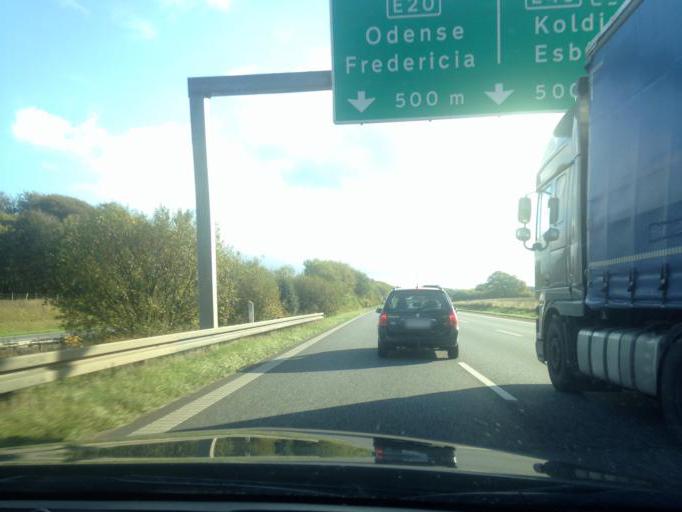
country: DK
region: South Denmark
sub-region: Vejle Kommune
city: Borkop
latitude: 55.6091
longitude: 9.5834
